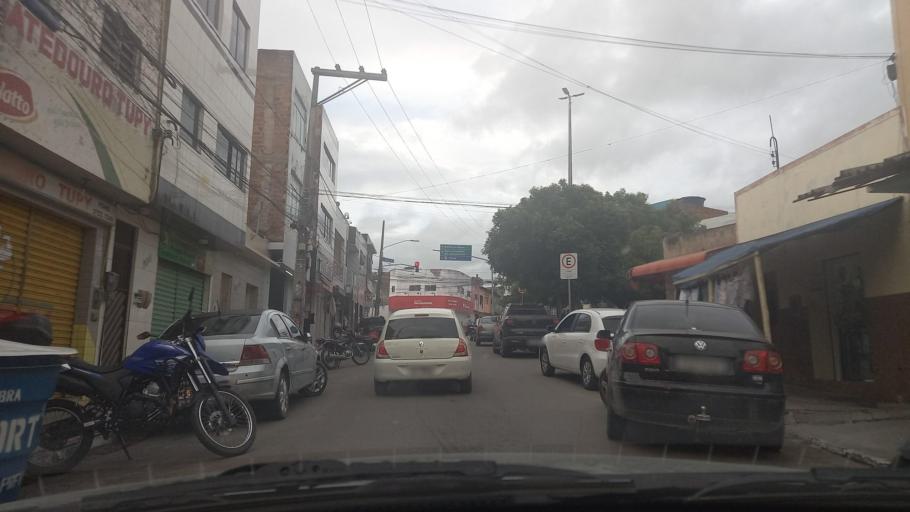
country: BR
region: Pernambuco
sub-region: Caruaru
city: Caruaru
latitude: -8.2789
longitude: -35.9658
